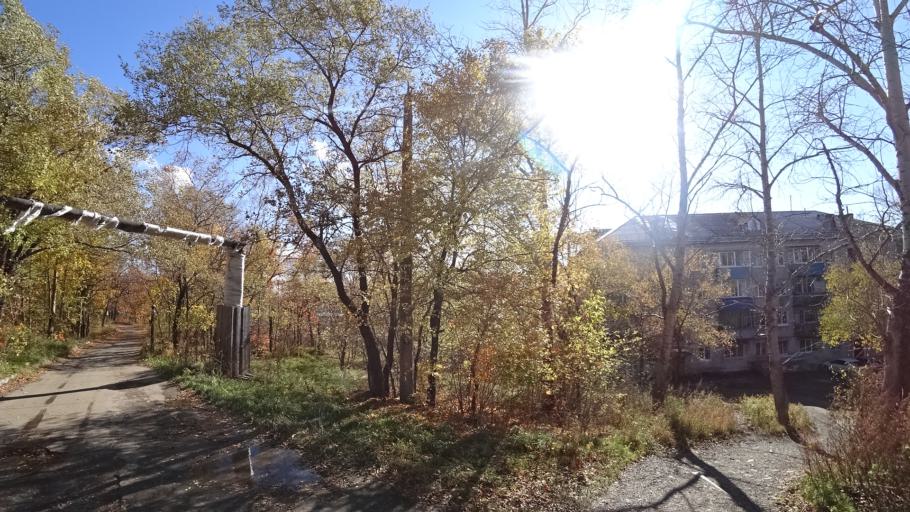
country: RU
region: Khabarovsk Krai
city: Amursk
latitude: 50.2193
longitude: 136.9059
